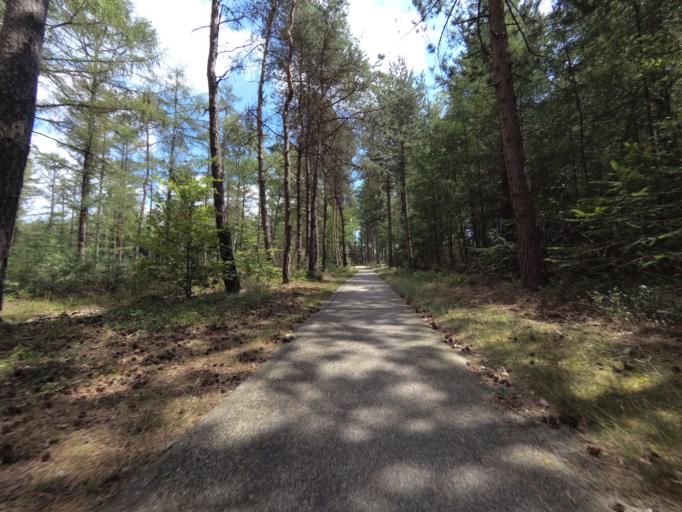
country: NL
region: Overijssel
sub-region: Gemeente Hof van Twente
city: Markelo
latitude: 52.3143
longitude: 6.4221
